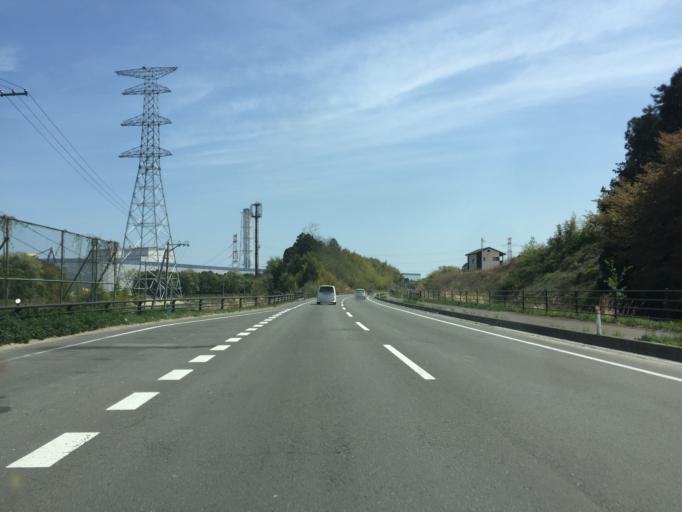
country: JP
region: Miyagi
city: Marumori
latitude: 37.8479
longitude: 140.9321
